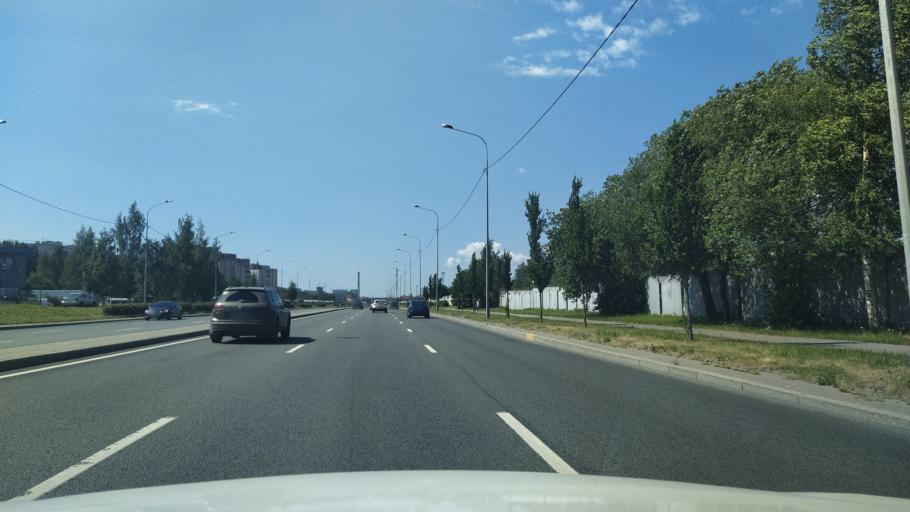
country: RU
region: Leningrad
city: Bugry
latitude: 60.0541
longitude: 30.3734
